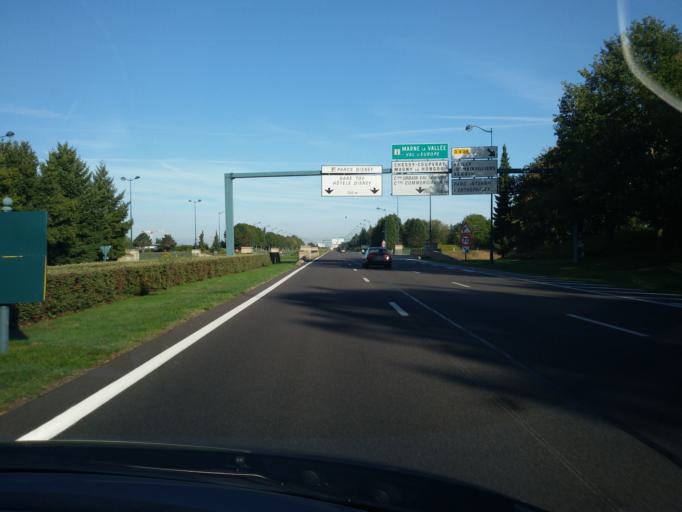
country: FR
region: Ile-de-France
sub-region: Departement de Seine-et-Marne
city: Bailly-Romainvilliers
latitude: 48.8469
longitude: 2.8103
